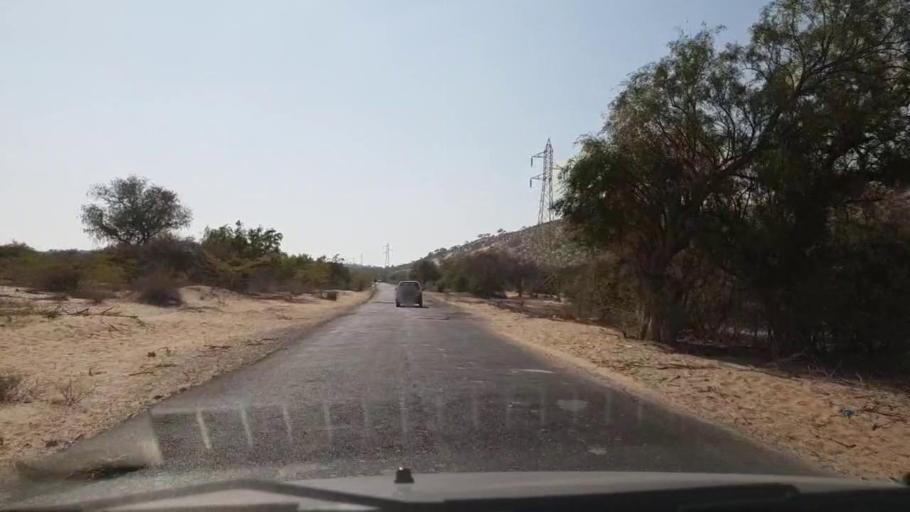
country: PK
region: Sindh
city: Mithi
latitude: 24.6430
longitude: 69.7459
